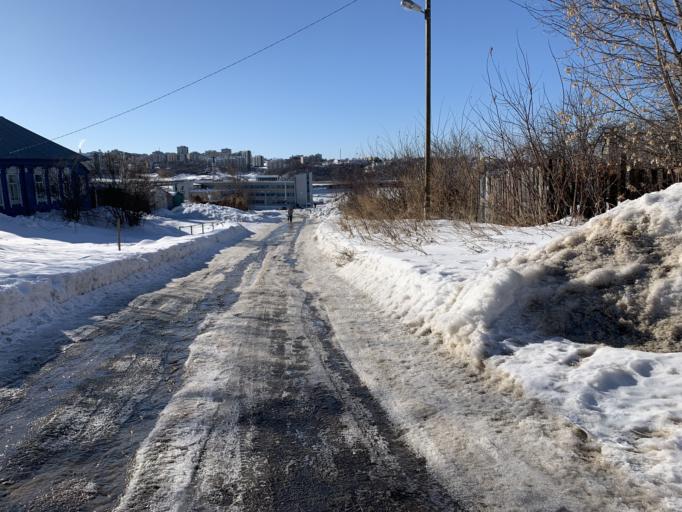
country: RU
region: Chuvashia
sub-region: Cheboksarskiy Rayon
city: Cheboksary
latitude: 56.1466
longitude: 47.2617
